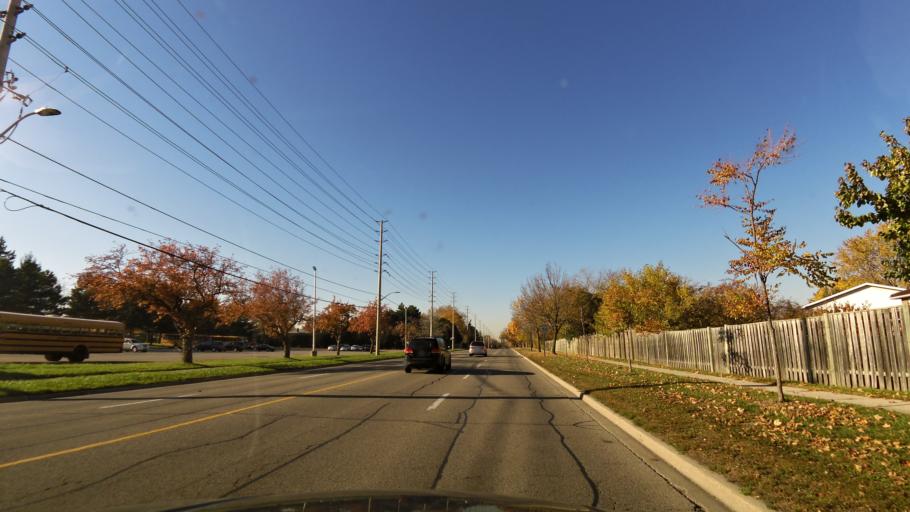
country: CA
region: Ontario
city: Etobicoke
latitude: 43.6084
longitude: -79.6047
